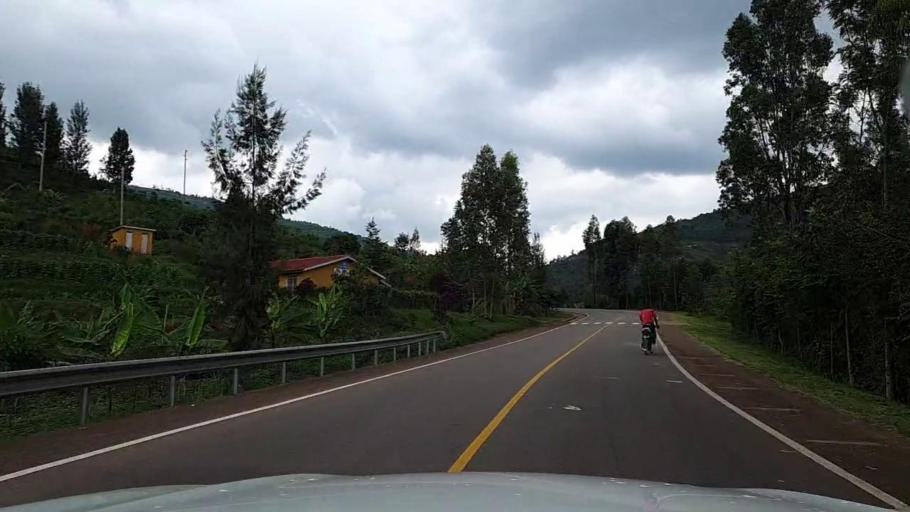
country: RW
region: Northern Province
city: Byumba
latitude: -1.6769
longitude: 30.0976
